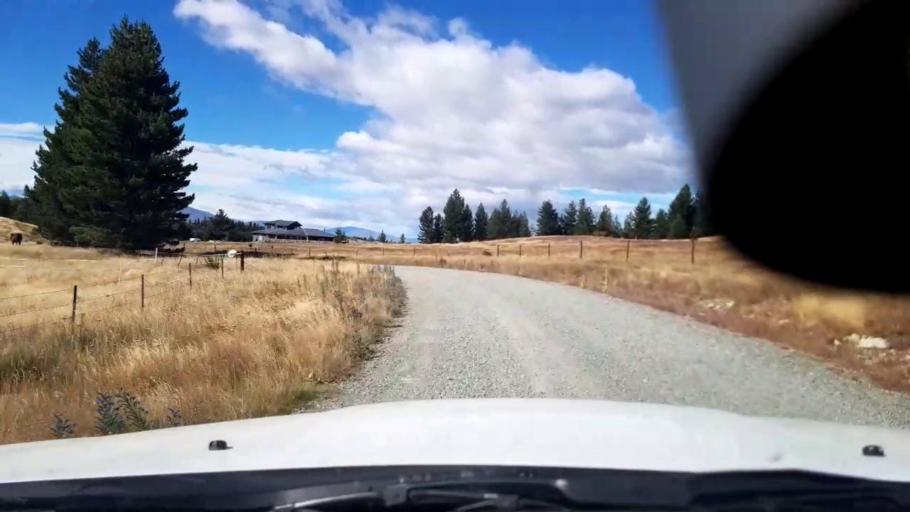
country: NZ
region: Canterbury
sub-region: Timaru District
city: Pleasant Point
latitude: -44.0104
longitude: 170.4723
